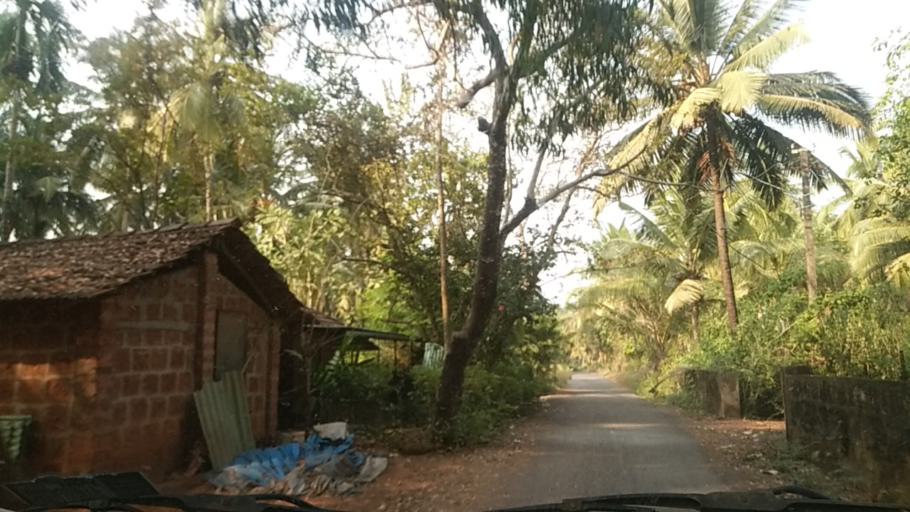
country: IN
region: Goa
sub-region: South Goa
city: Colva
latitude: 15.3100
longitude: 73.9318
